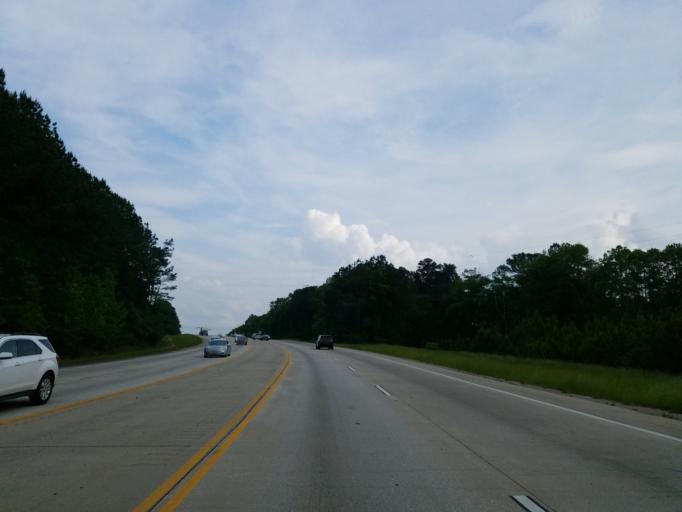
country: US
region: Georgia
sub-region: Cobb County
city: Powder Springs
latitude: 33.8517
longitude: -84.6973
